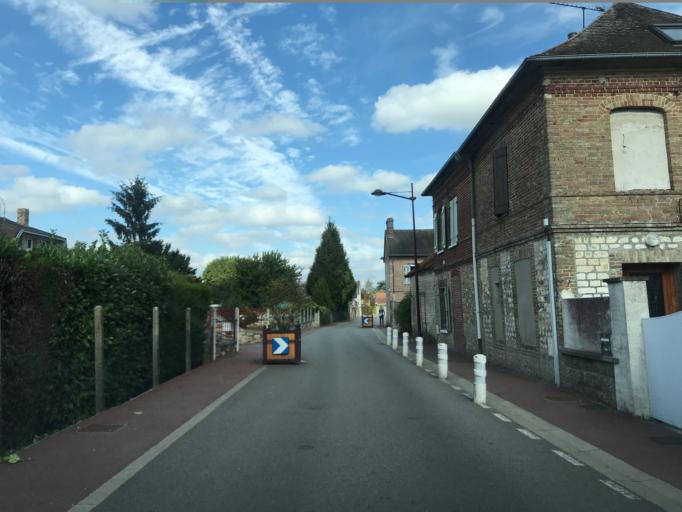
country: FR
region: Haute-Normandie
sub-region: Departement de l'Eure
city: Le Vaudreuil
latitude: 49.2524
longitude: 1.1972
